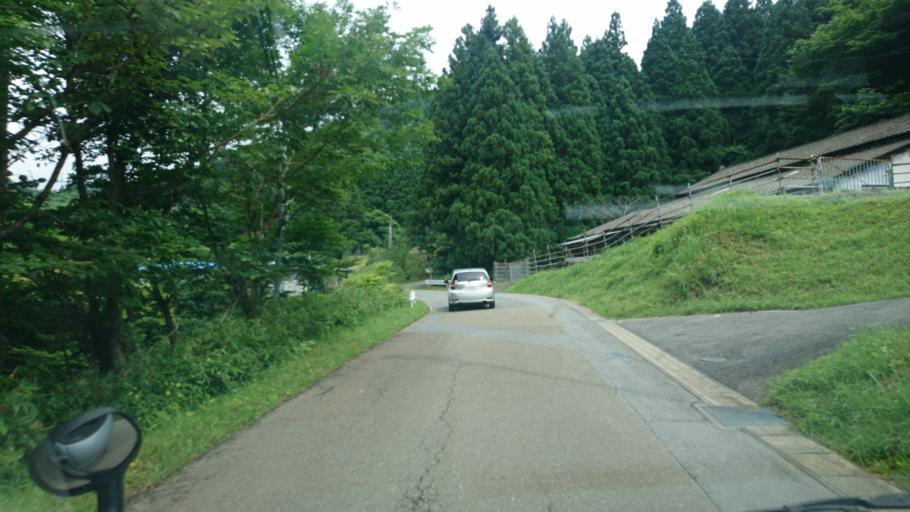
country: JP
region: Iwate
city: Ofunato
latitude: 39.1310
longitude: 141.7988
